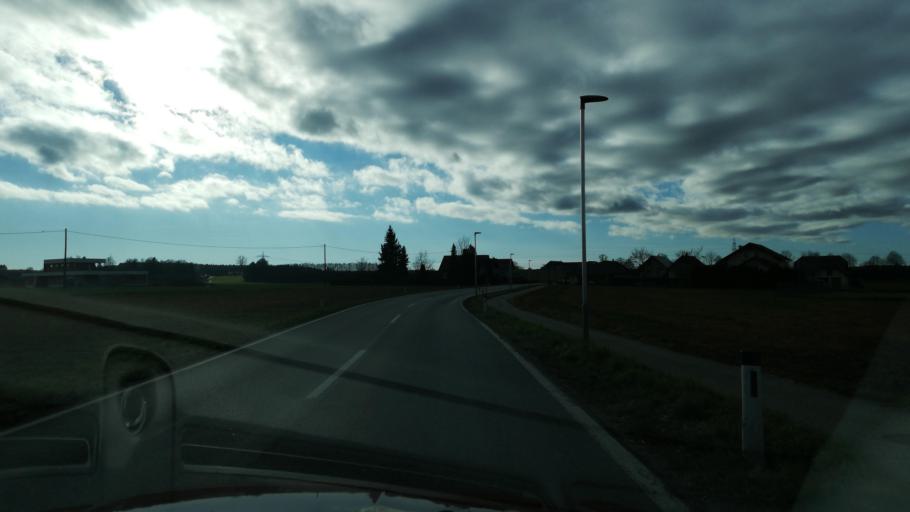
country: AT
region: Upper Austria
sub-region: Politischer Bezirk Braunau am Inn
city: Braunau am Inn
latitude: 48.2021
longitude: 13.0988
